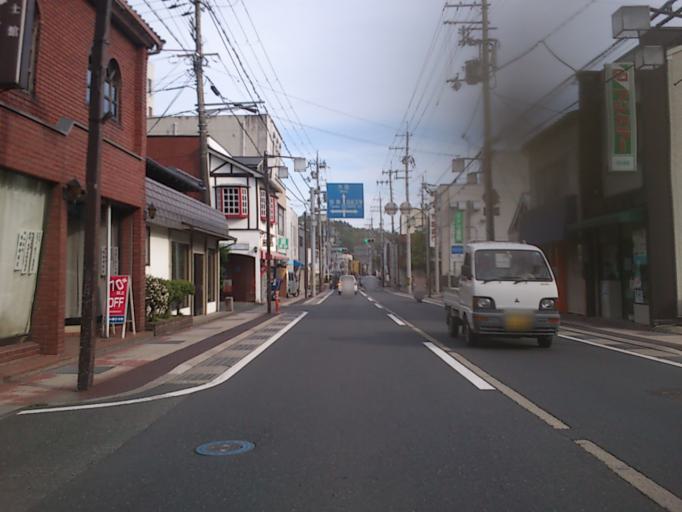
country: JP
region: Kyoto
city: Miyazu
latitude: 35.6256
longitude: 135.0576
